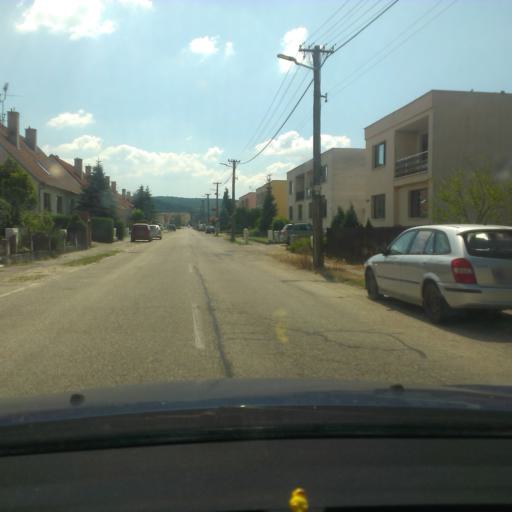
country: SK
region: Trnavsky
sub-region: Okres Trnava
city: Piestany
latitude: 48.5407
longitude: 17.8429
